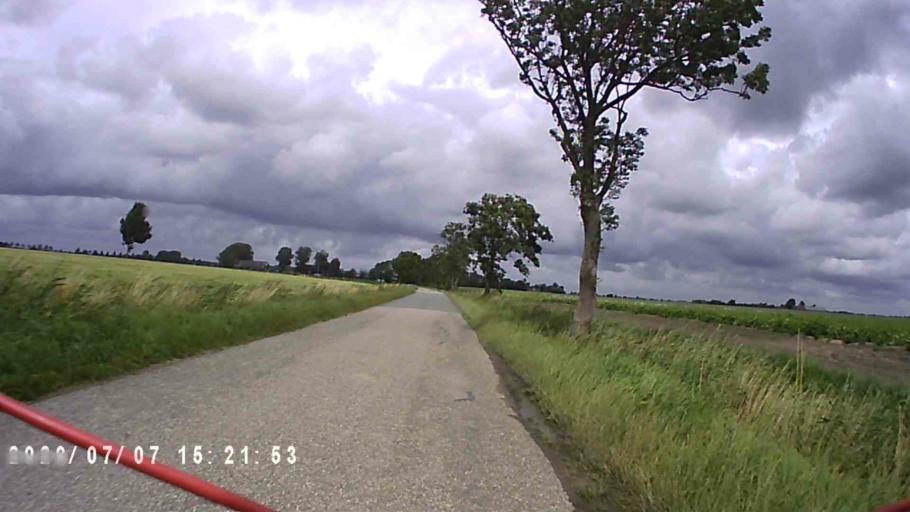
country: NL
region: Groningen
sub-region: Gemeente Winsum
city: Winsum
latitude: 53.3414
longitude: 6.4561
